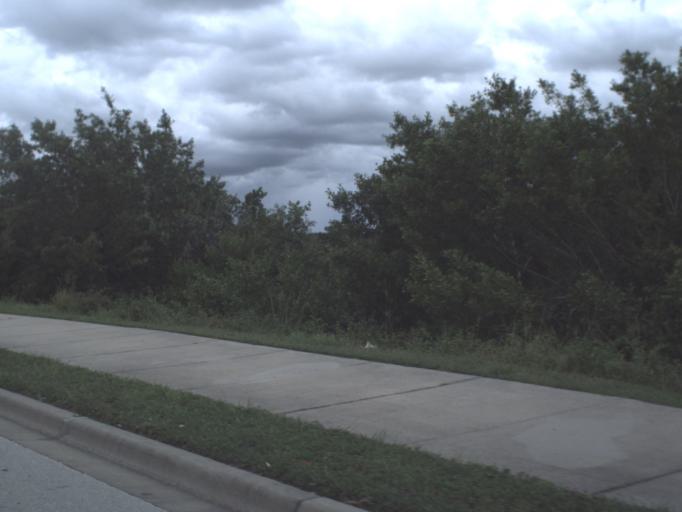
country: US
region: Florida
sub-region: Sarasota County
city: Nokomis
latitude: 27.1180
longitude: -82.4507
